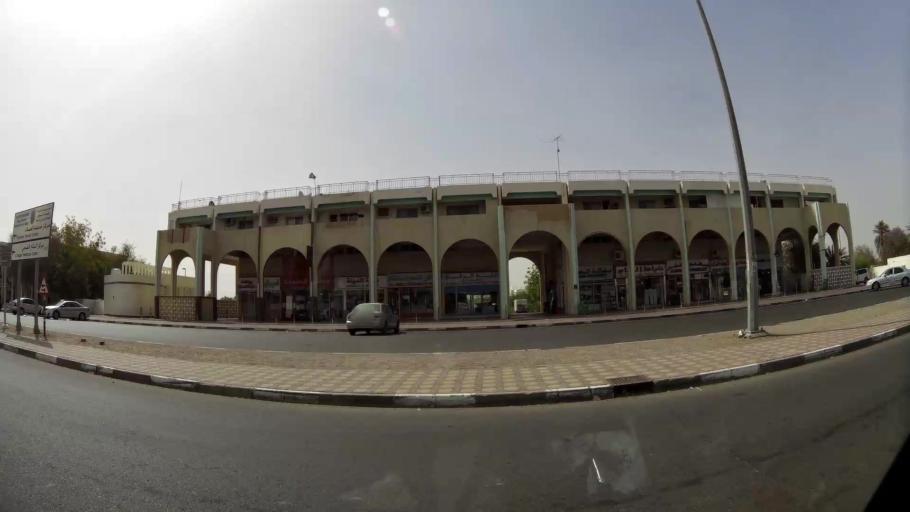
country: AE
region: Abu Dhabi
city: Al Ain
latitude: 24.1848
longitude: 55.6285
